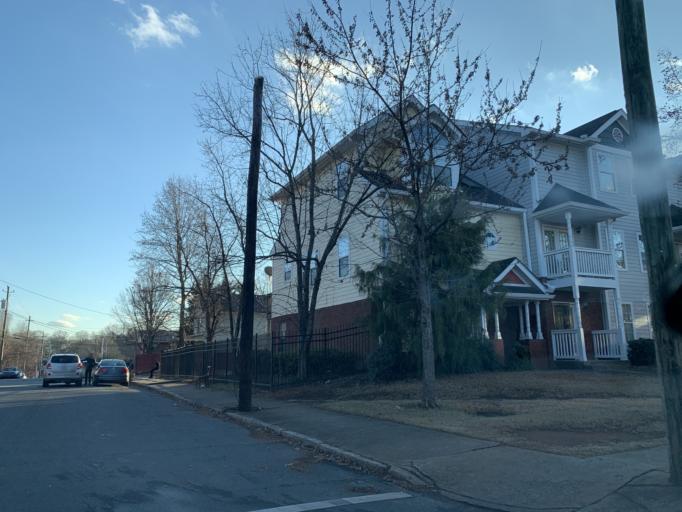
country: US
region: Georgia
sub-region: Fulton County
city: Atlanta
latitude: 33.7381
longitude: -84.3971
